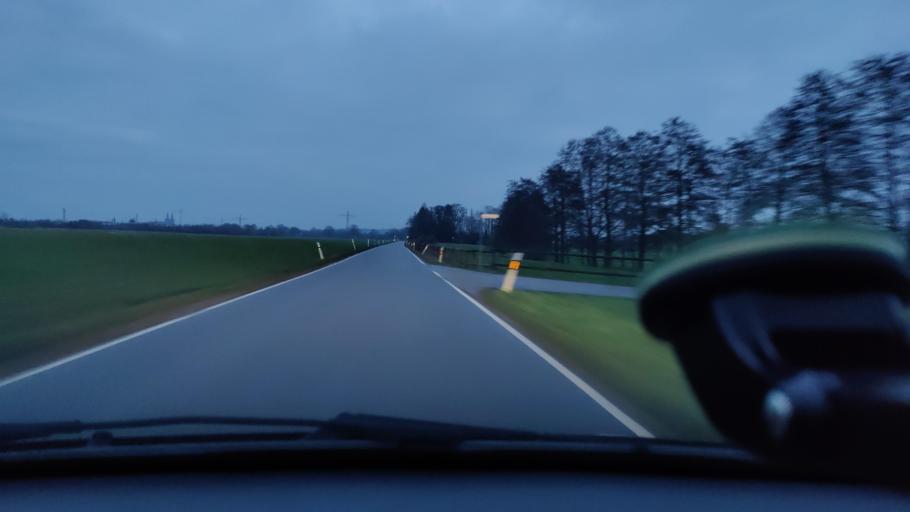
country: DE
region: North Rhine-Westphalia
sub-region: Regierungsbezirk Dusseldorf
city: Xanten
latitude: 51.6639
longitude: 6.4153
